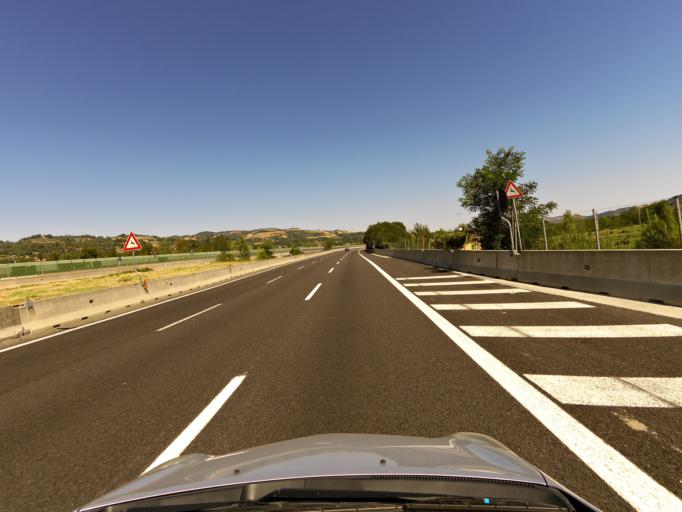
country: IT
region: Emilia-Romagna
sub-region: Provincia di Bologna
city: Sasso Marconi
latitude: 44.3908
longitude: 11.2597
